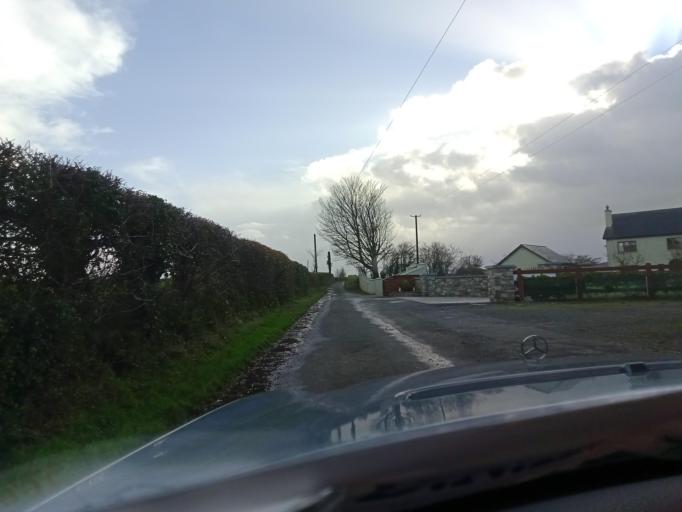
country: IE
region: Leinster
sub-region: Kilkenny
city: Mooncoin
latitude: 52.2885
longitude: -7.2729
